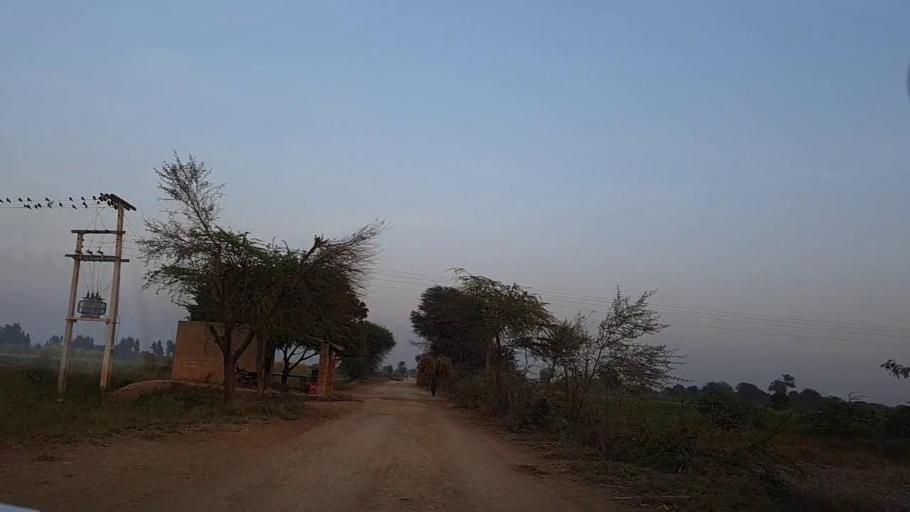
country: PK
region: Sindh
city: Tando Ghulam Ali
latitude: 25.1573
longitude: 68.9259
